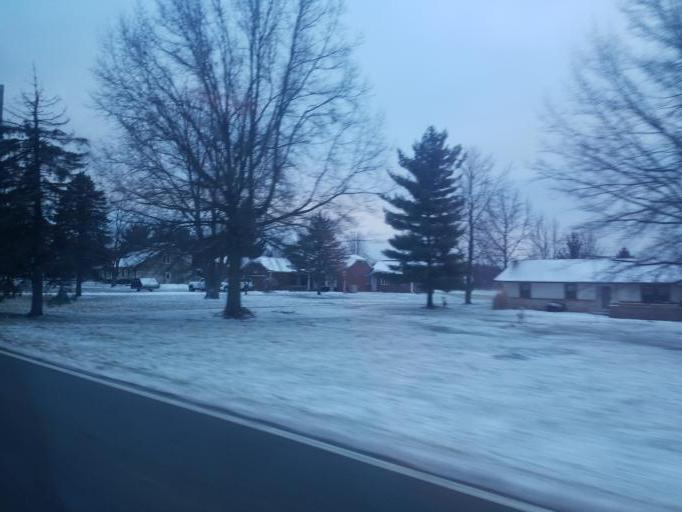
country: US
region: Ohio
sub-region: Franklin County
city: New Albany
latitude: 40.1295
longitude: -82.8459
